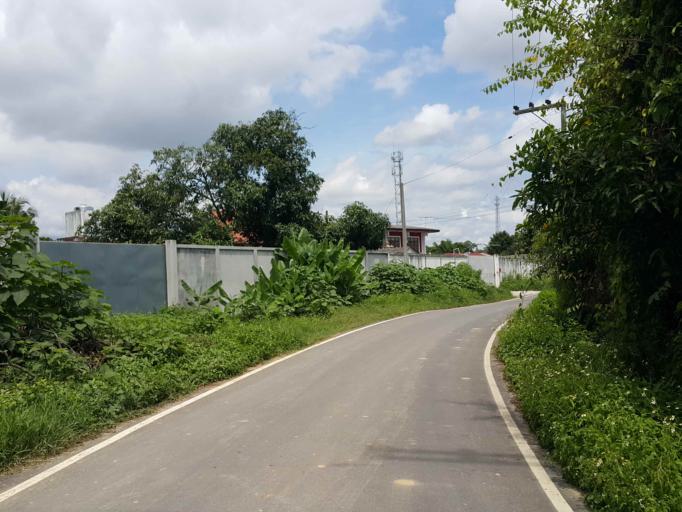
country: TH
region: Chiang Mai
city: San Sai
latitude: 18.8063
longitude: 99.0489
